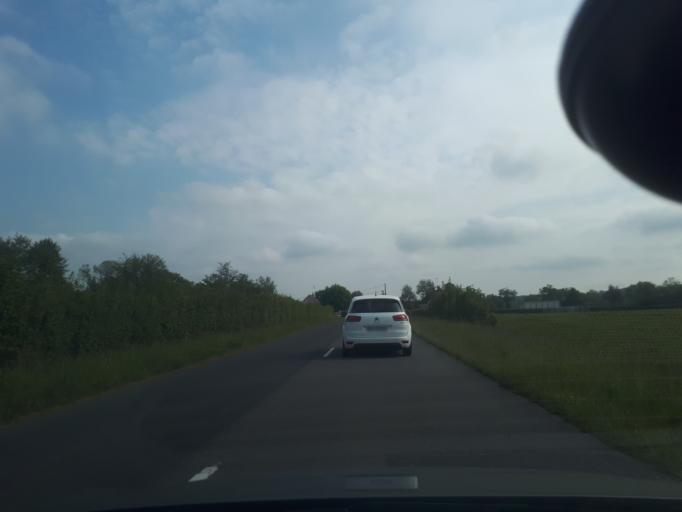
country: FR
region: Auvergne
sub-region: Departement de l'Allier
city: Dompierre-sur-Besbre
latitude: 46.4365
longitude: 3.6239
